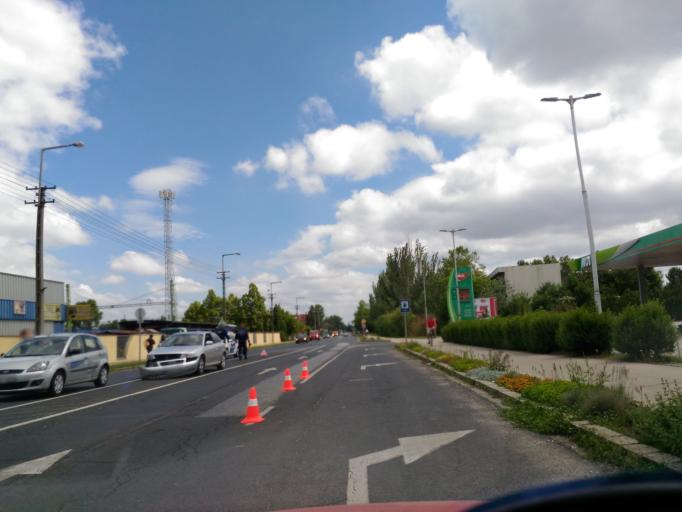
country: HU
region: Fejer
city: Gardony
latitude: 47.2041
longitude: 18.6221
